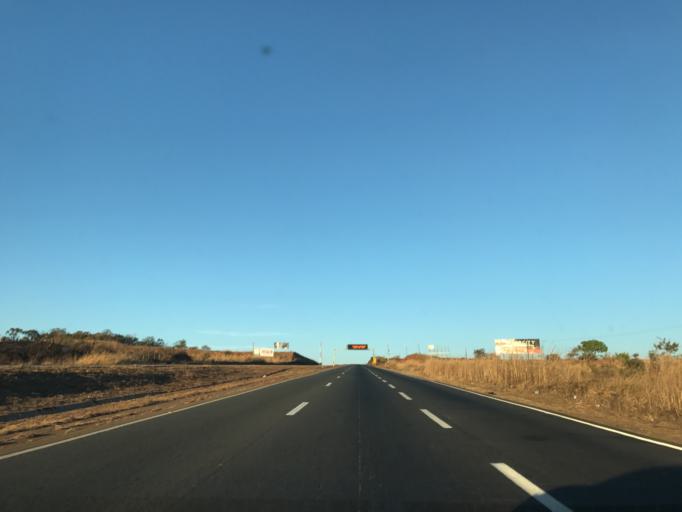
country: BR
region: Goias
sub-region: Anapolis
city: Anapolis
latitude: -16.3284
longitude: -48.8844
